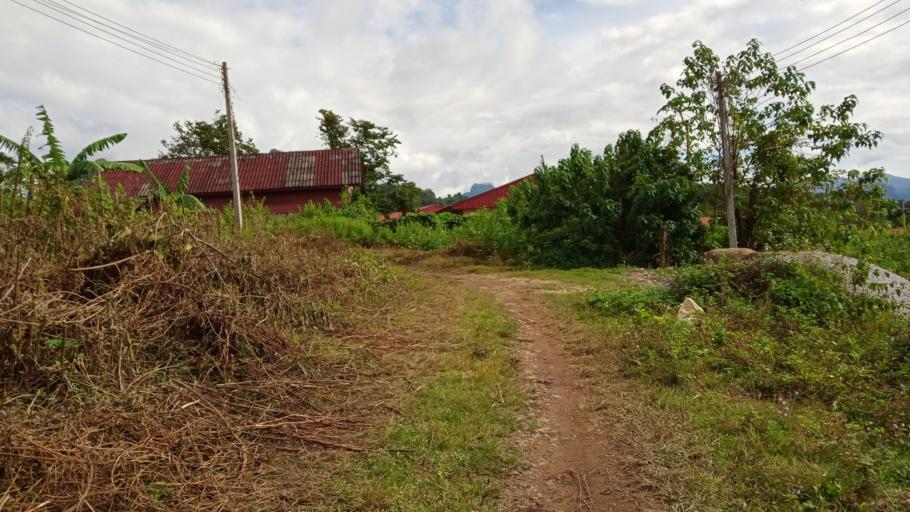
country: LA
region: Xiangkhoang
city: Phonsavan
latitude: 19.1050
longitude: 102.9289
